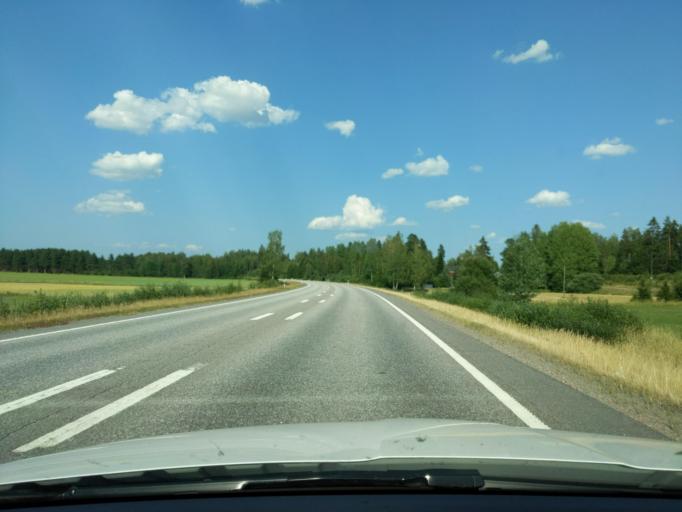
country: FI
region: Haeme
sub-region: Riihimaeki
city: Oitti
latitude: 60.7992
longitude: 25.0321
